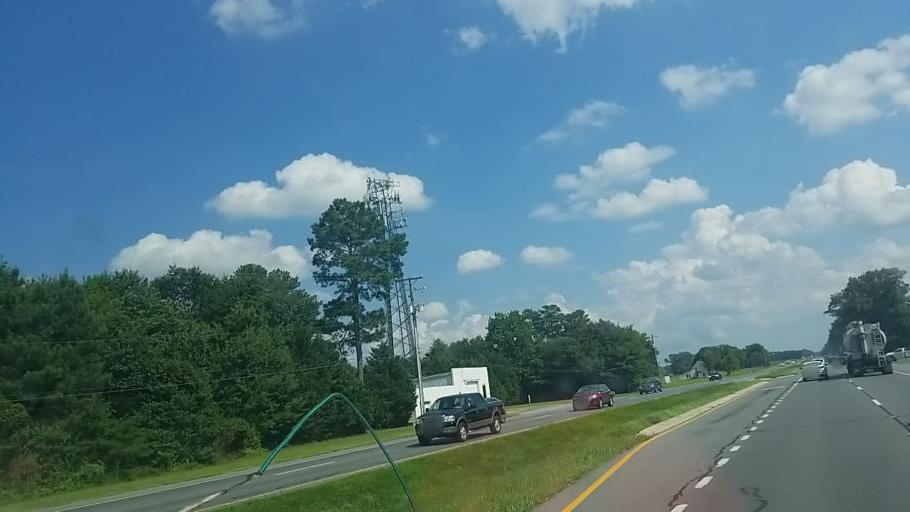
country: US
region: Delaware
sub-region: Sussex County
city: Millsboro
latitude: 38.6309
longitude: -75.3473
